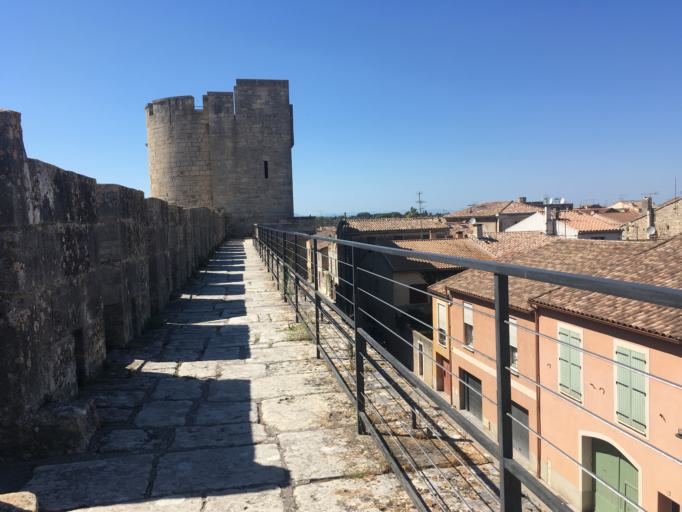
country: FR
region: Languedoc-Roussillon
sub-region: Departement du Gard
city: Aigues-Mortes
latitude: 43.5650
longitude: 4.1902
